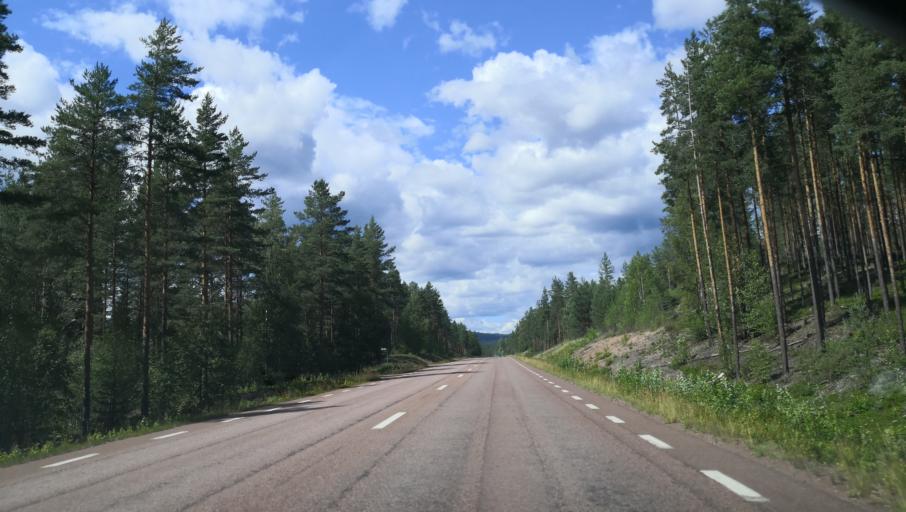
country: SE
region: Dalarna
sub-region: Alvdalens Kommun
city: AElvdalen
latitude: 61.2629
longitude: 14.0172
